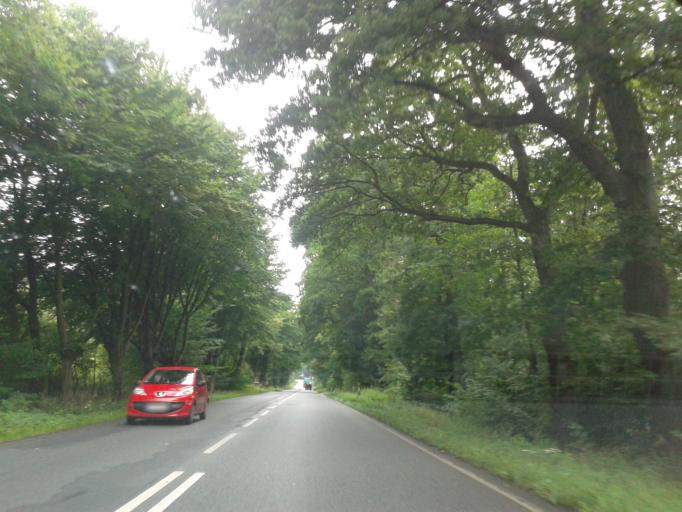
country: DE
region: North Rhine-Westphalia
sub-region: Regierungsbezirk Detmold
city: Blomberg
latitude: 51.9557
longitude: 9.1161
